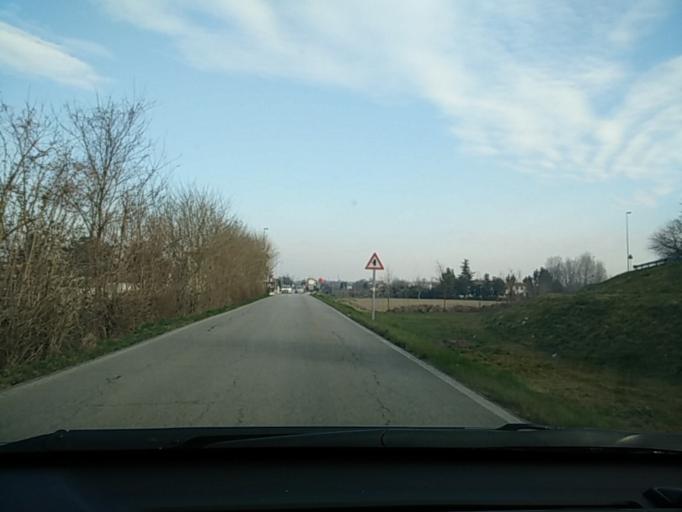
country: IT
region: Veneto
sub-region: Provincia di Venezia
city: Fossalta di Piave
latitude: 45.6511
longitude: 12.5121
